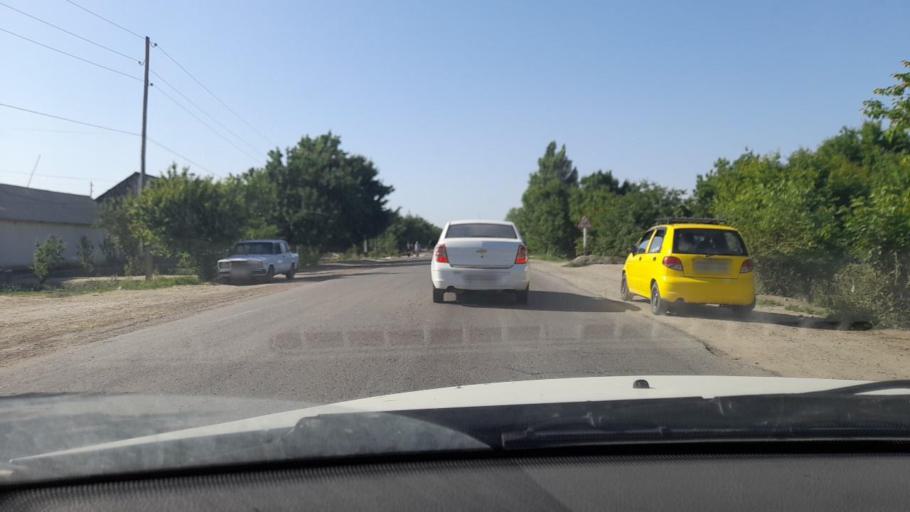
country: UZ
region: Bukhara
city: Romiton
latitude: 40.0592
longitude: 64.3276
